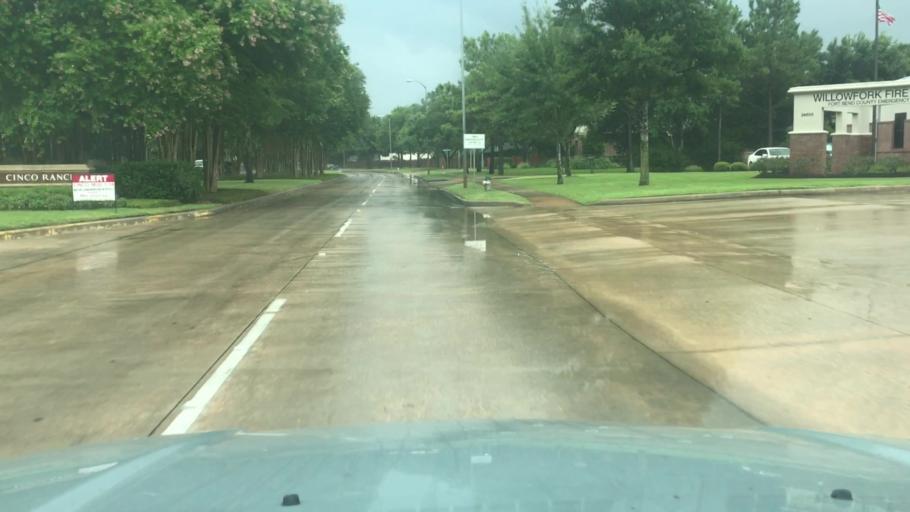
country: US
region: Texas
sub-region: Fort Bend County
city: Cinco Ranch
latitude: 29.7411
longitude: -95.7879
